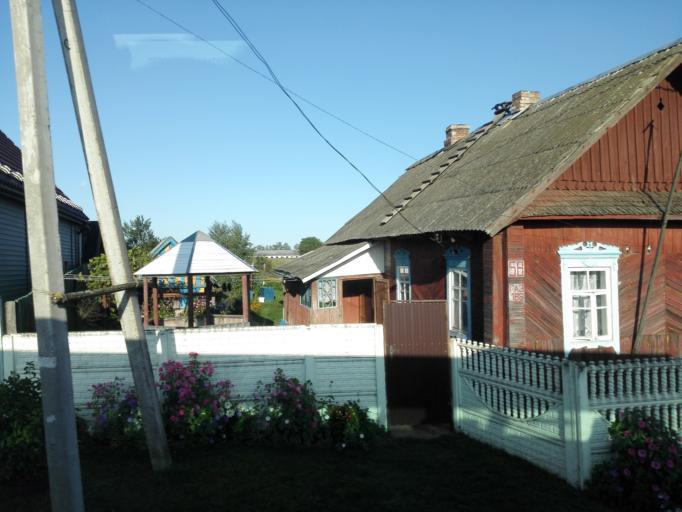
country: BY
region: Mogilev
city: Yalizava
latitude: 53.3251
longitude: 29.0503
